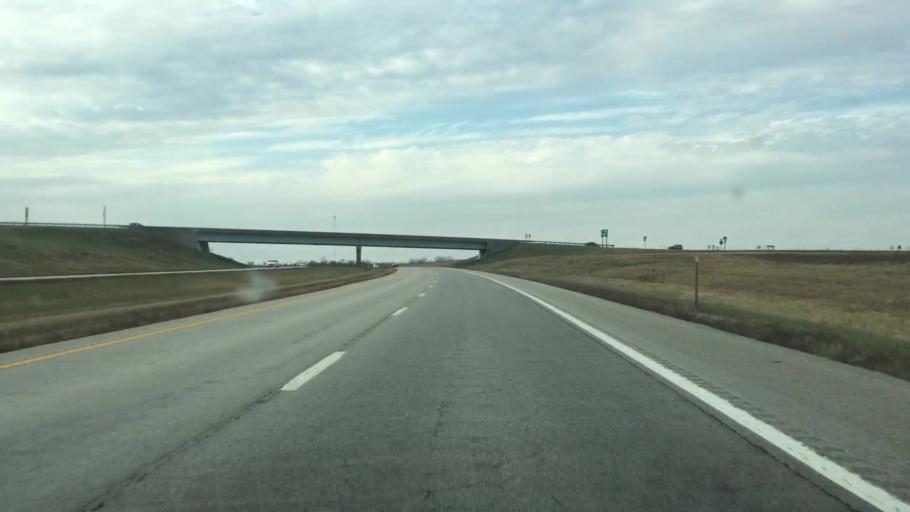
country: US
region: Missouri
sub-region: Cass County
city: Garden City
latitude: 38.5712
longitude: -94.1910
